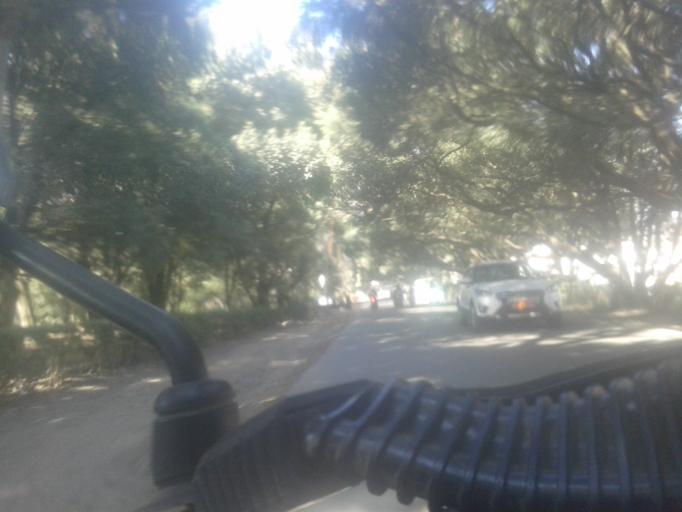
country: NP
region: Central Region
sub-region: Bagmati Zone
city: Patan
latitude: 27.6792
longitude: 85.2961
